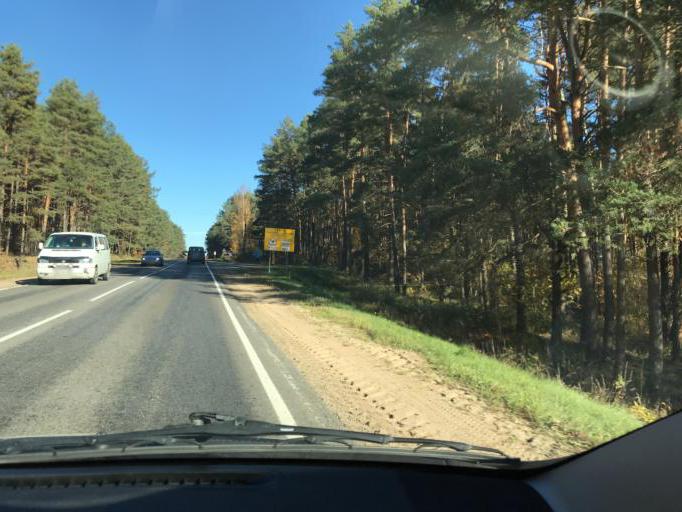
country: BY
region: Vitebsk
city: Polatsk
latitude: 55.3173
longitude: 28.7776
